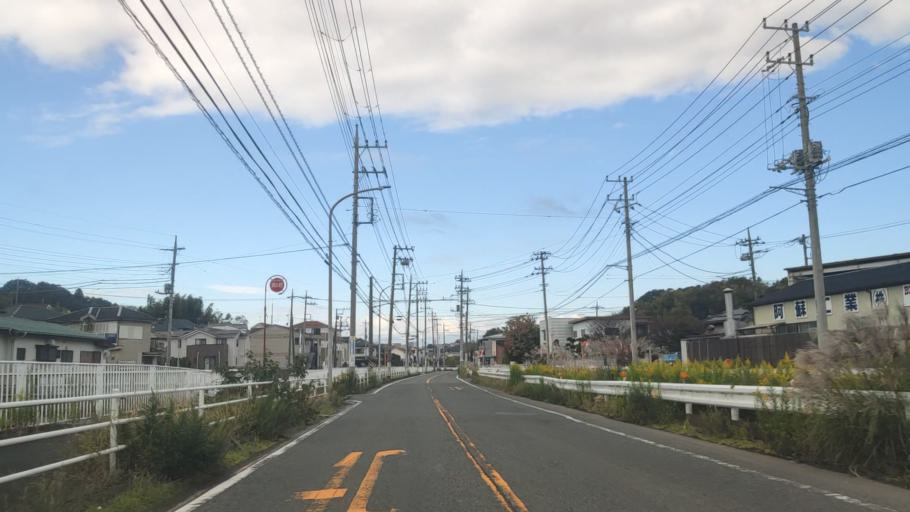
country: JP
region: Kanagawa
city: Minami-rinkan
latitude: 35.4270
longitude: 139.5230
